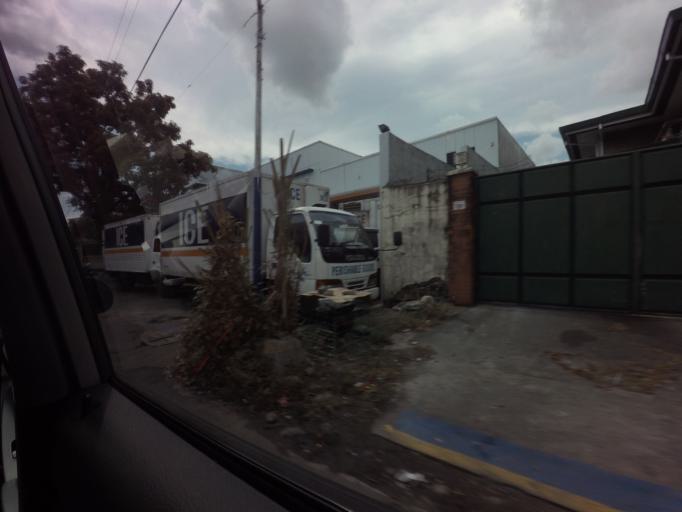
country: PH
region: Metro Manila
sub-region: City of Manila
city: Quiapo
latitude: 14.6037
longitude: 121.0076
